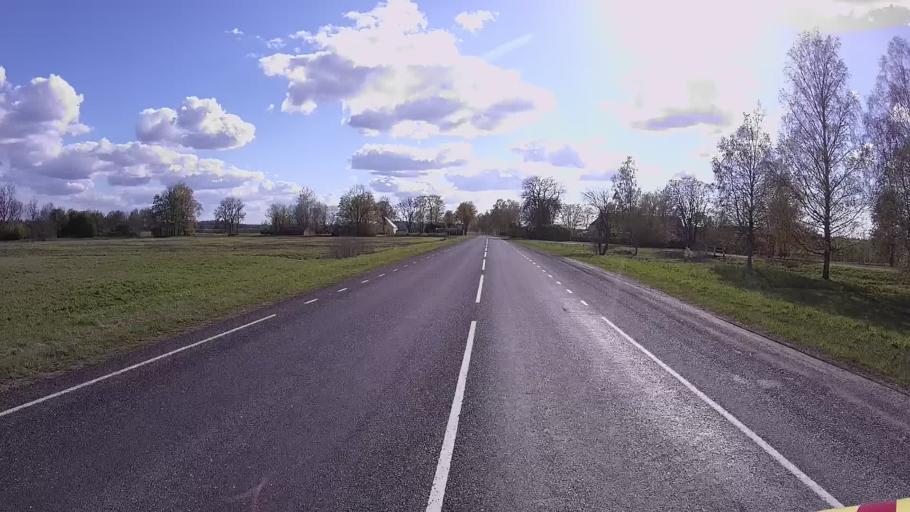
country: EE
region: Jogevamaa
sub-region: Jogeva linn
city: Jogeva
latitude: 58.7294
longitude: 26.2008
